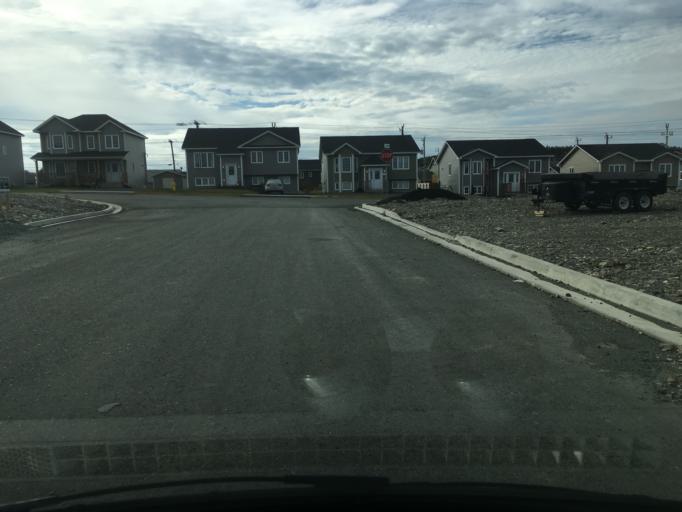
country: CA
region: Newfoundland and Labrador
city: Mount Pearl
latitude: 47.5517
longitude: -52.7891
